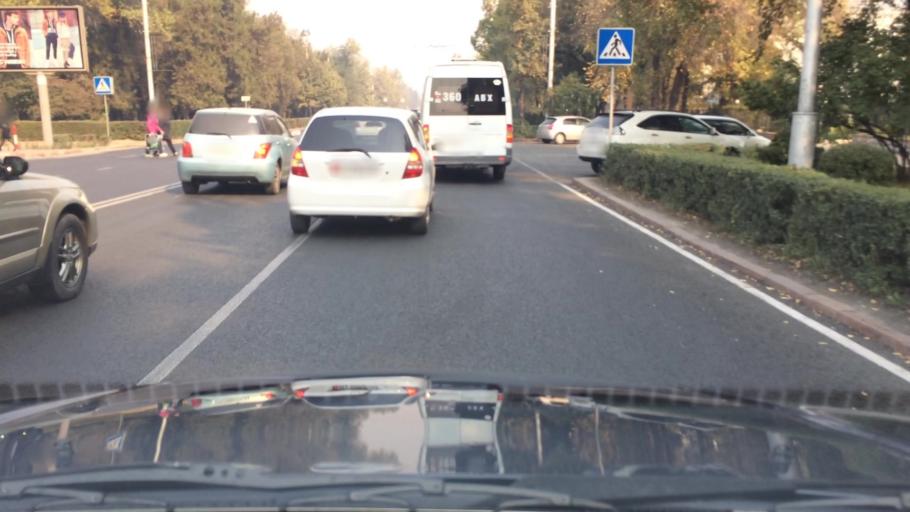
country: KG
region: Chuy
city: Bishkek
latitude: 42.8447
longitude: 74.5862
